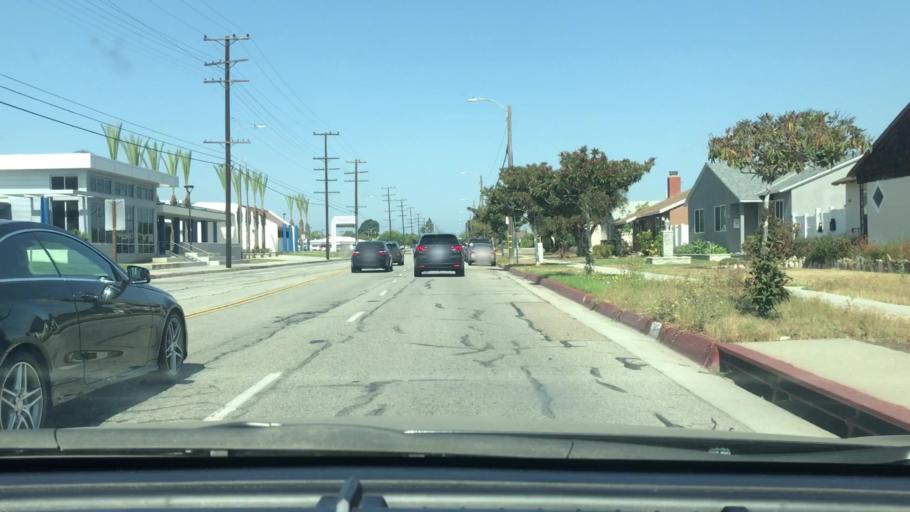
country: US
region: California
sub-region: Los Angeles County
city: Alondra Park
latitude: 33.8656
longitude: -118.3355
